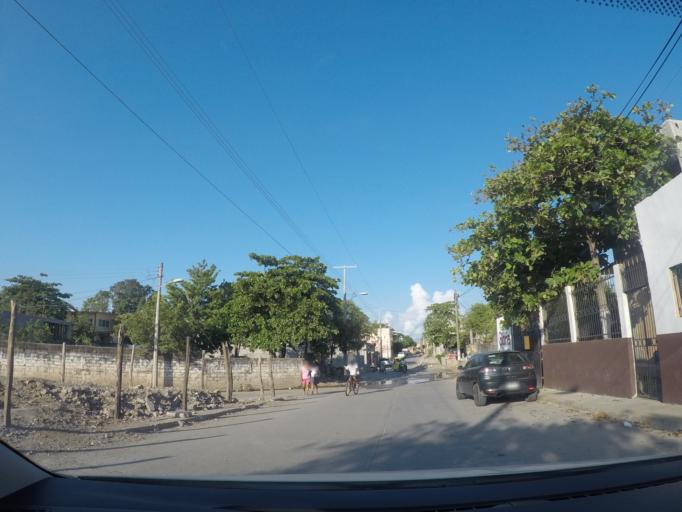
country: MX
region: Oaxaca
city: Juchitan de Zaragoza
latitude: 16.4394
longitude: -95.0291
